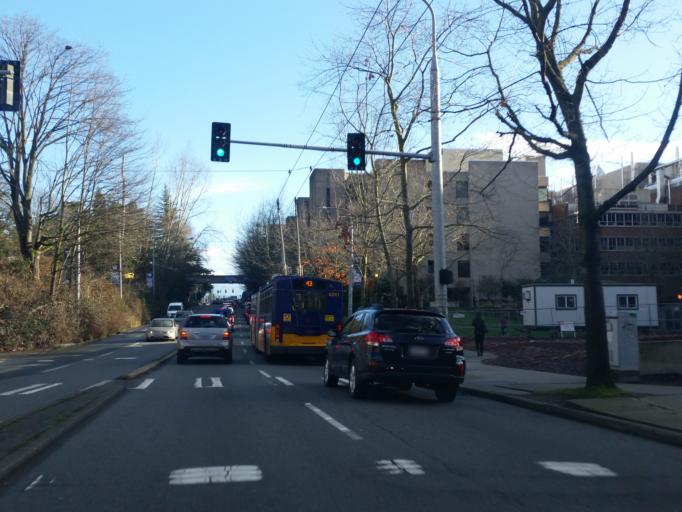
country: US
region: Washington
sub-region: King County
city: Seattle
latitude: 47.6522
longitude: -122.3109
